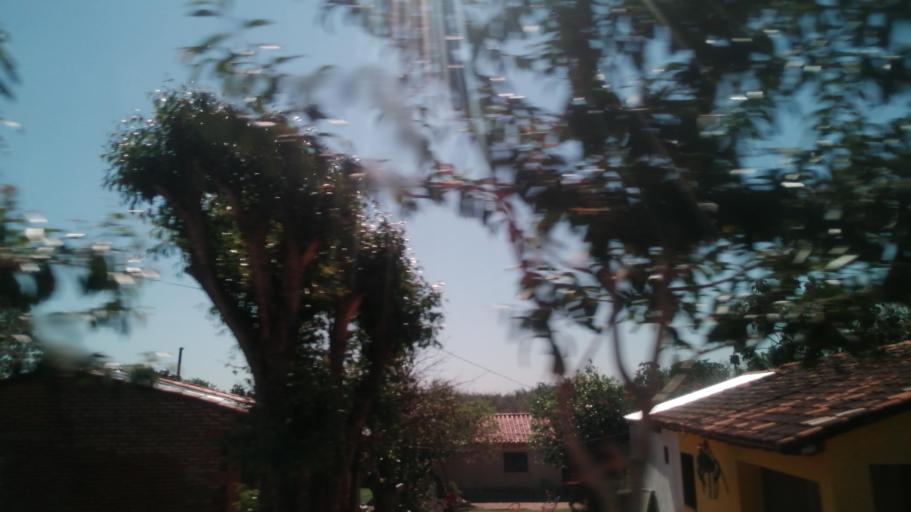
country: PY
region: Misiones
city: San Juan Bautista
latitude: -26.6627
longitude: -57.1479
